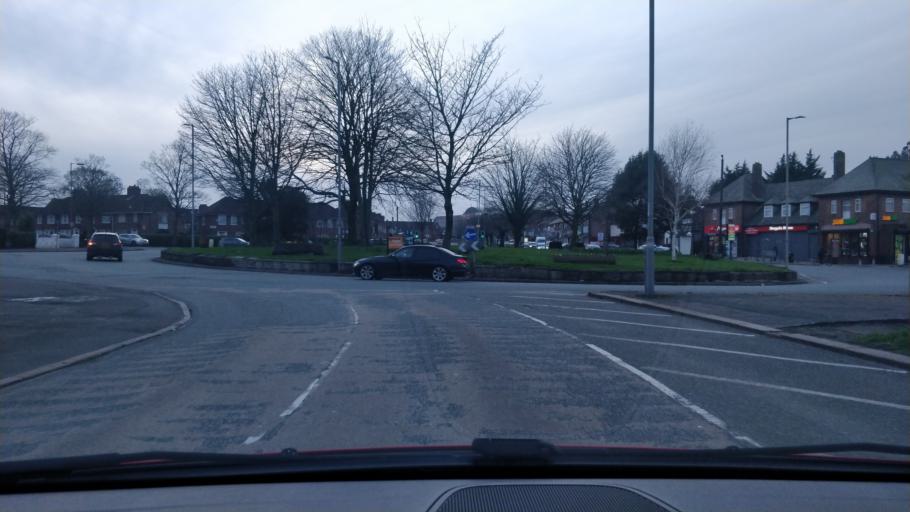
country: GB
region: England
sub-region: Knowsley
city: Knowsley
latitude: 53.4189
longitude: -2.8878
